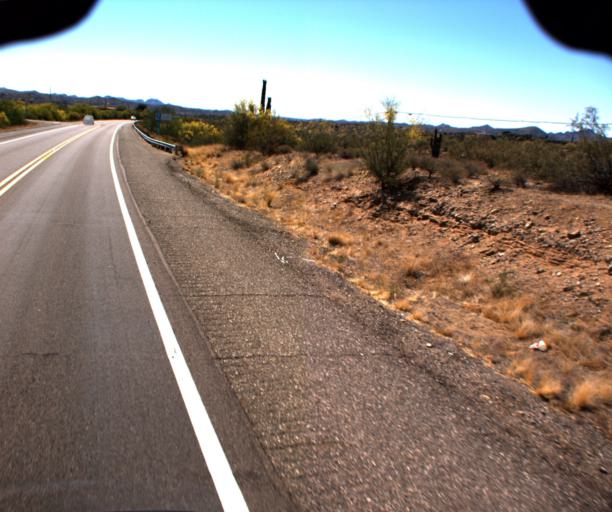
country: US
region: Arizona
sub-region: Maricopa County
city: Wickenburg
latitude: 33.9982
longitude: -112.7593
